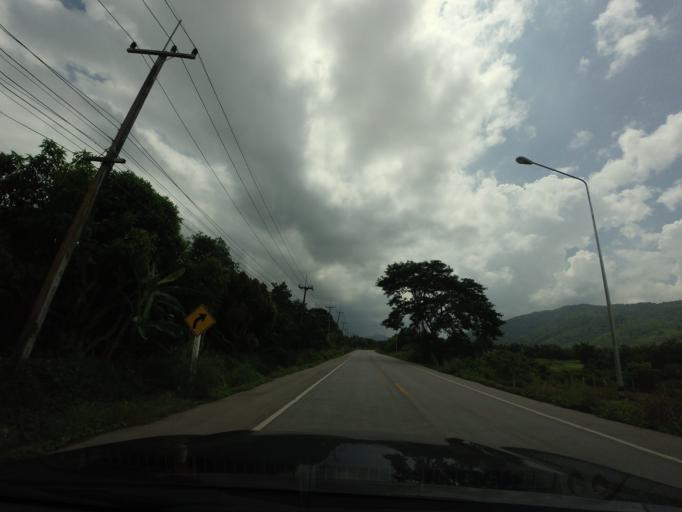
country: TH
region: Loei
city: Pak Chom
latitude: 18.0255
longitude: 101.7654
